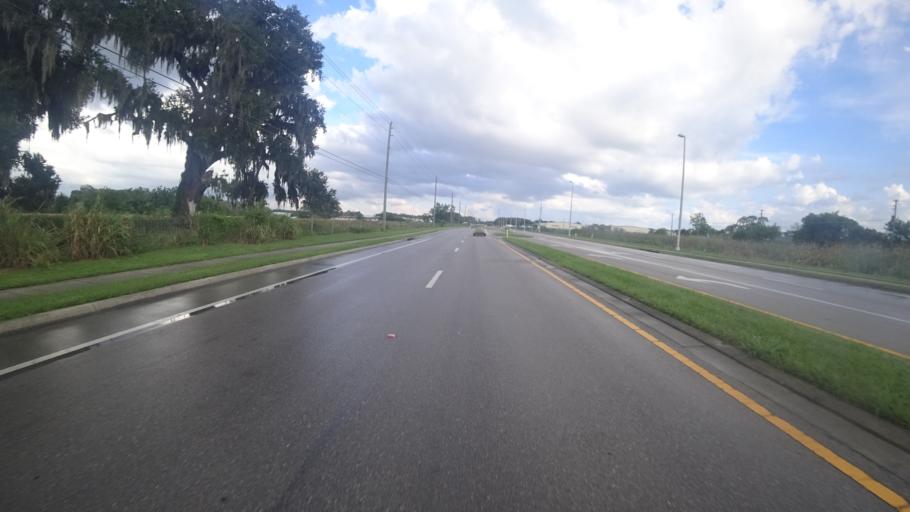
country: US
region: Florida
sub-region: Manatee County
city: Memphis
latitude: 27.5285
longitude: -82.5557
